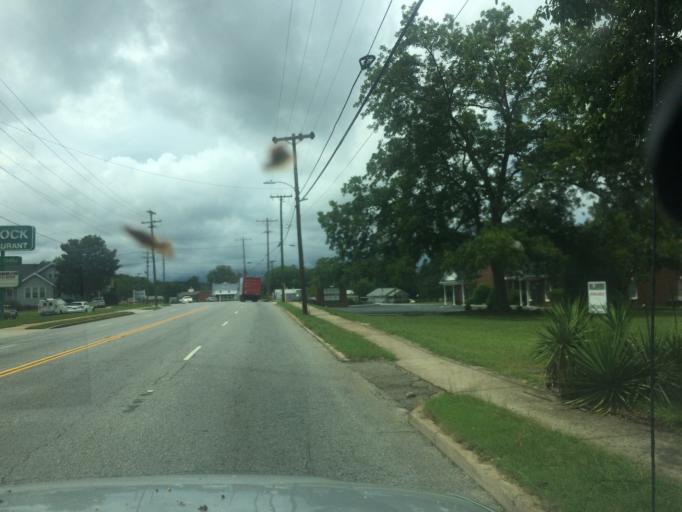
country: US
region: South Carolina
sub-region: Greenville County
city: Greer
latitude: 34.9419
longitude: -82.2366
